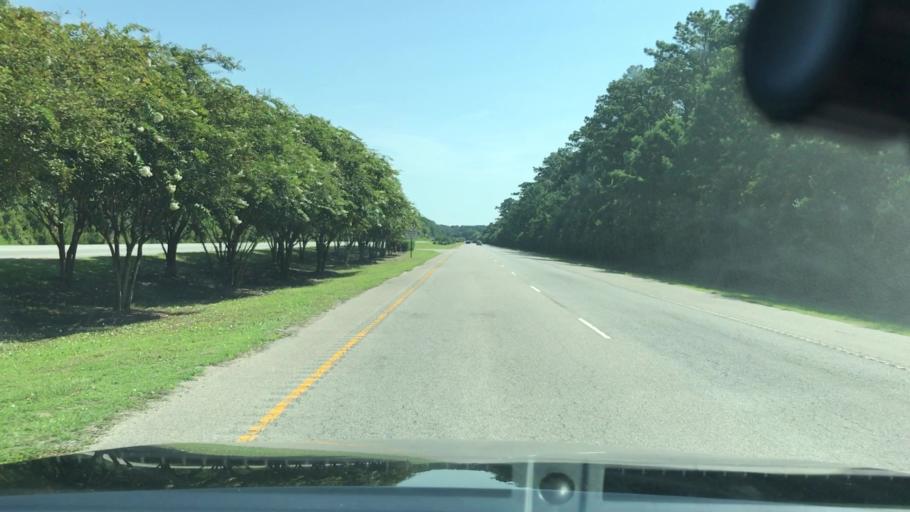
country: US
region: South Carolina
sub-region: Beaufort County
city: Hilton Head Island
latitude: 32.2018
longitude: -80.7516
